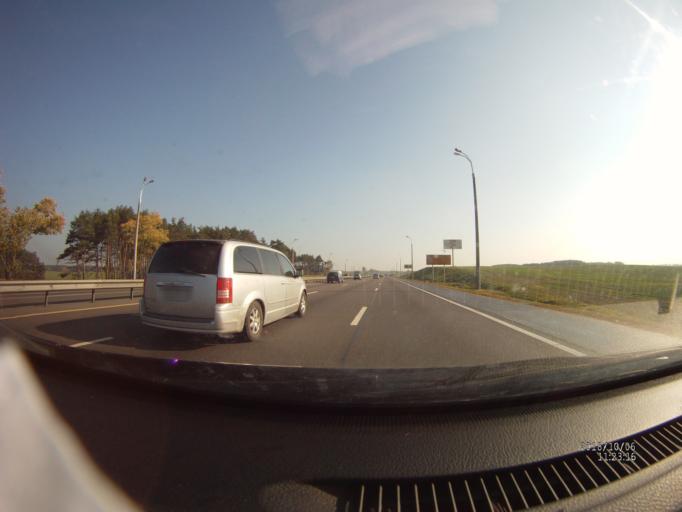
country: BY
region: Minsk
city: Bal'shavik
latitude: 53.9702
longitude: 27.5708
